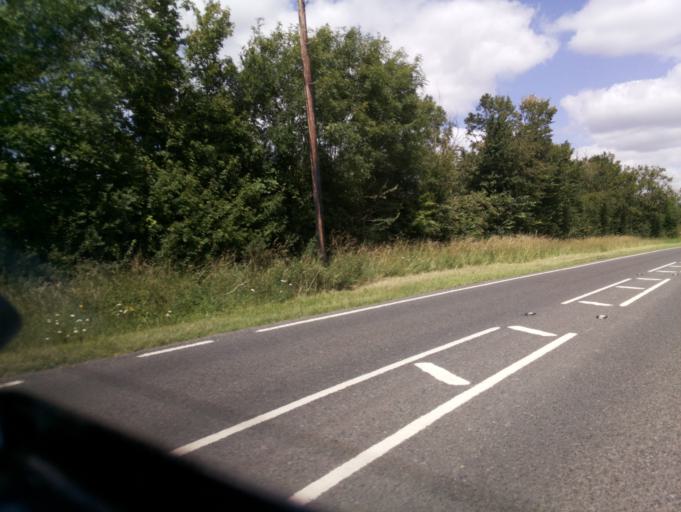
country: GB
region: England
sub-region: Buckinghamshire
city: Aylesbury
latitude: 51.8685
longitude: -0.8332
